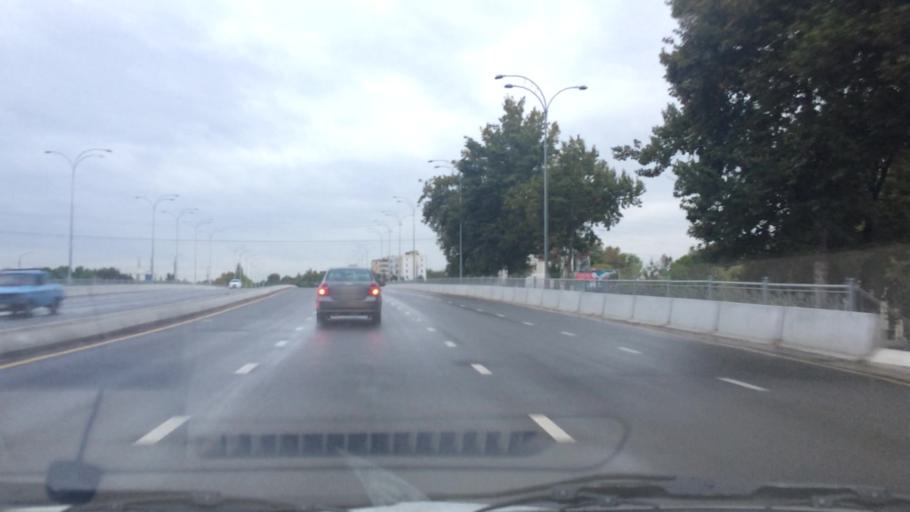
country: UZ
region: Toshkent Shahri
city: Tashkent
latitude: 41.2760
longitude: 69.2059
